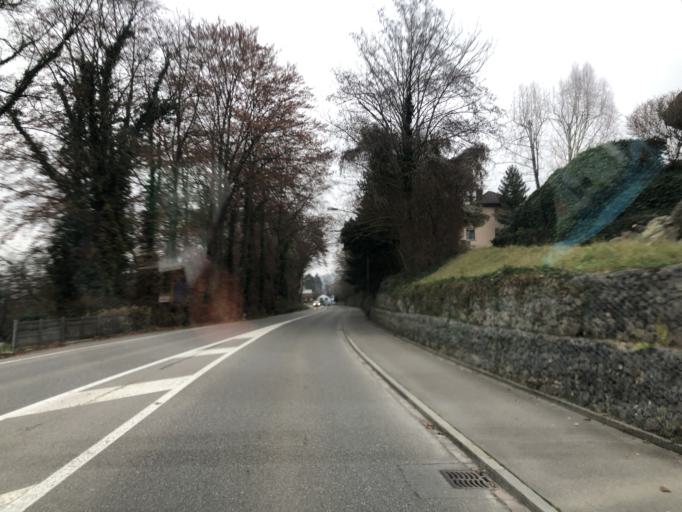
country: CH
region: Aargau
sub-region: Bezirk Baden
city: Turgi
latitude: 47.4896
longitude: 8.2522
